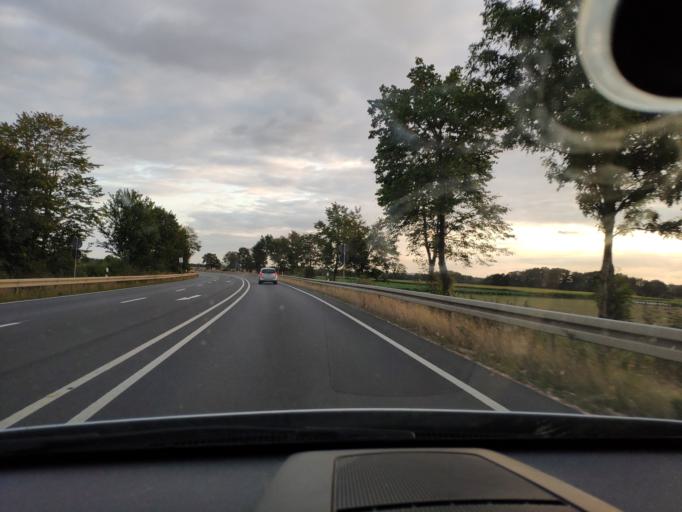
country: DE
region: North Rhine-Westphalia
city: Geilenkirchen
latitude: 50.9723
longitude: 6.0892
